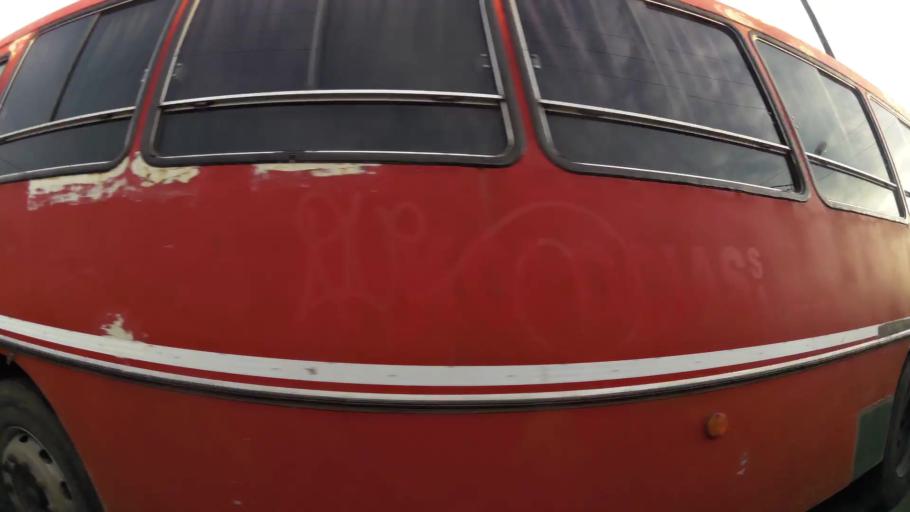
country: AR
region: Buenos Aires
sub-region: Partido de Almirante Brown
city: Adrogue
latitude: -34.7609
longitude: -58.3425
